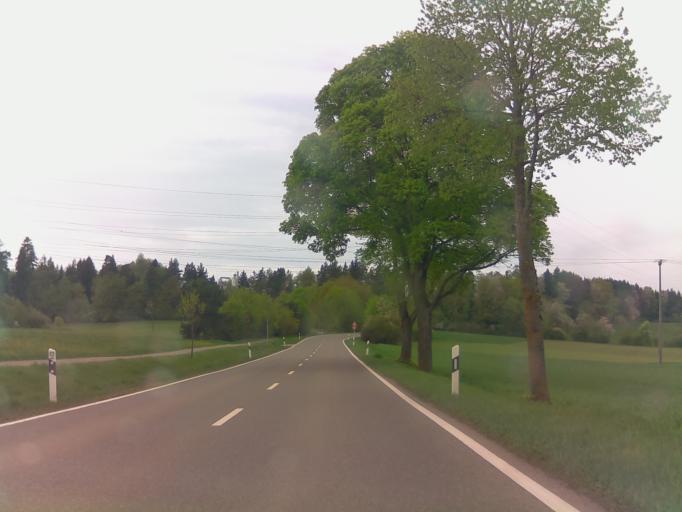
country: DE
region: Baden-Wuerttemberg
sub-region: Freiburg Region
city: Monchweiler
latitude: 48.0971
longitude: 8.4588
